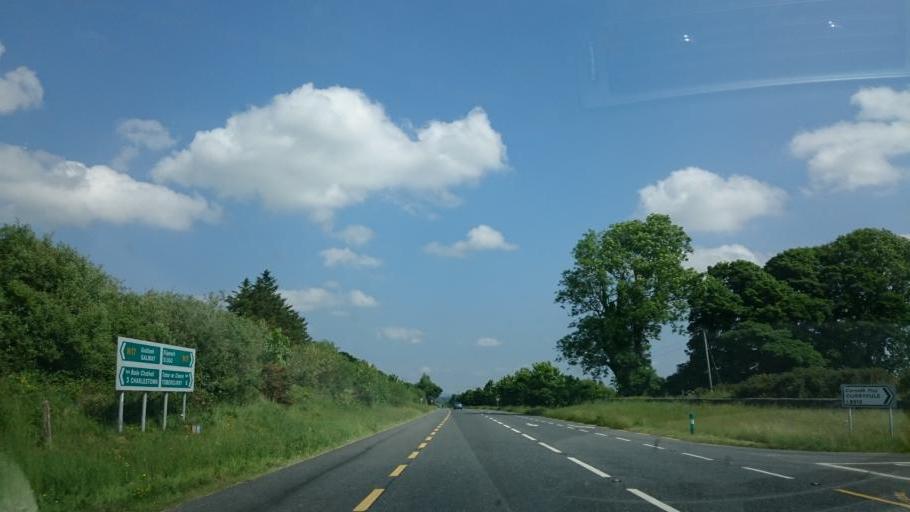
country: IE
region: Connaught
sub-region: Sligo
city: Tobercurry
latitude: 53.9900
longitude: -8.7798
